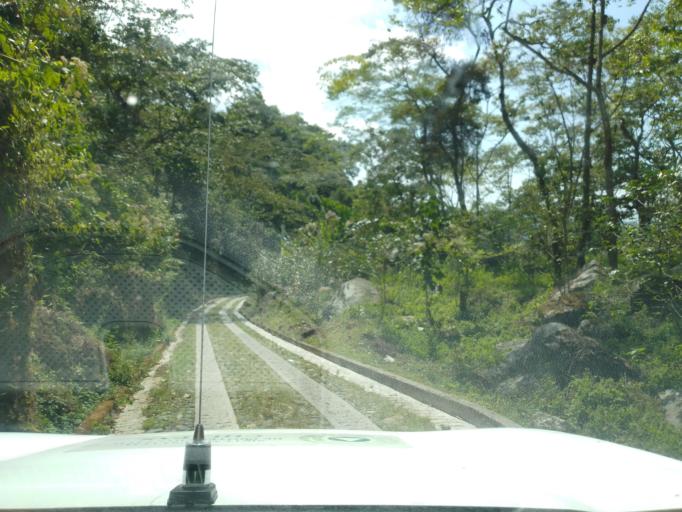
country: MX
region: Chiapas
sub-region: Union Juarez
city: Santo Domingo
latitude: 15.0718
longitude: -92.0913
